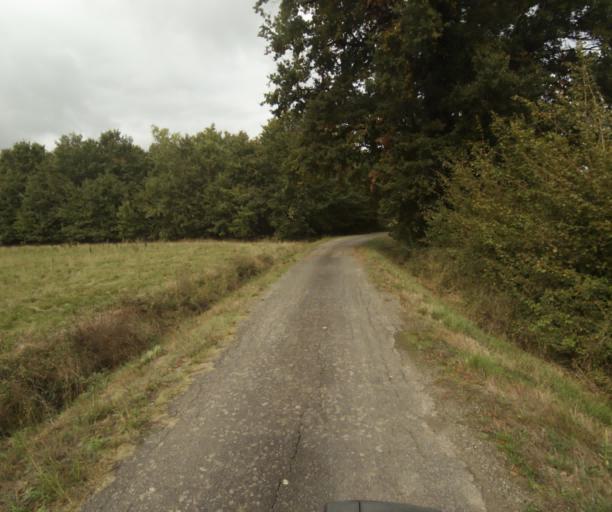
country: FR
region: Midi-Pyrenees
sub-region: Departement du Tarn-et-Garonne
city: Montech
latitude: 43.9744
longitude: 1.2527
